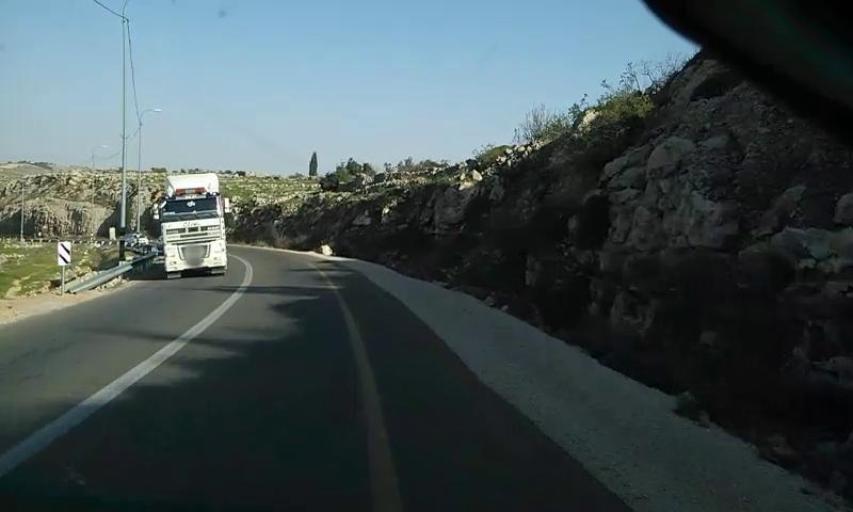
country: PS
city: Khallat ad Dar
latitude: 31.5010
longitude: 35.1126
